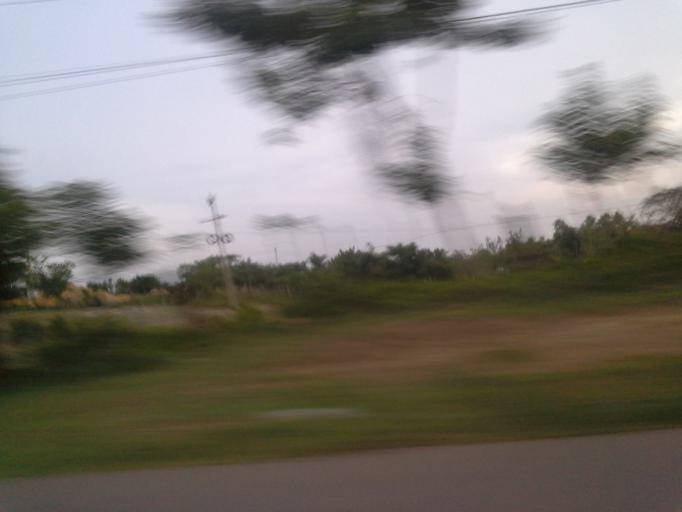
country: CO
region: Sucre
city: Los Palmitos
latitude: 9.3634
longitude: -75.2772
